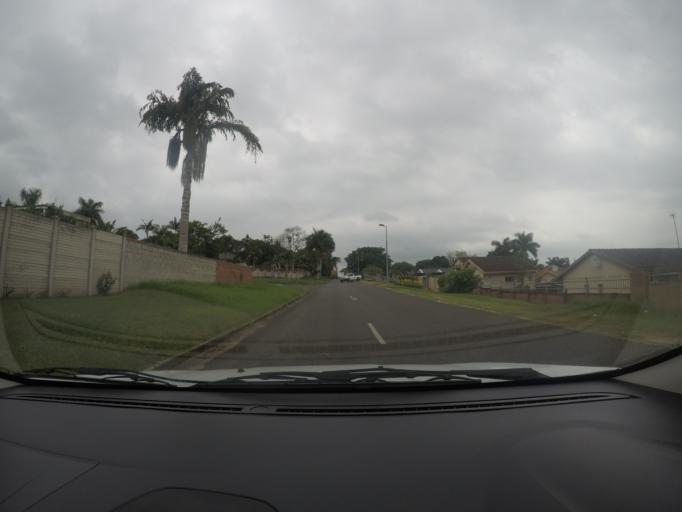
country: ZA
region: KwaZulu-Natal
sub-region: uThungulu District Municipality
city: Empangeni
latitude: -28.7351
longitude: 31.8995
